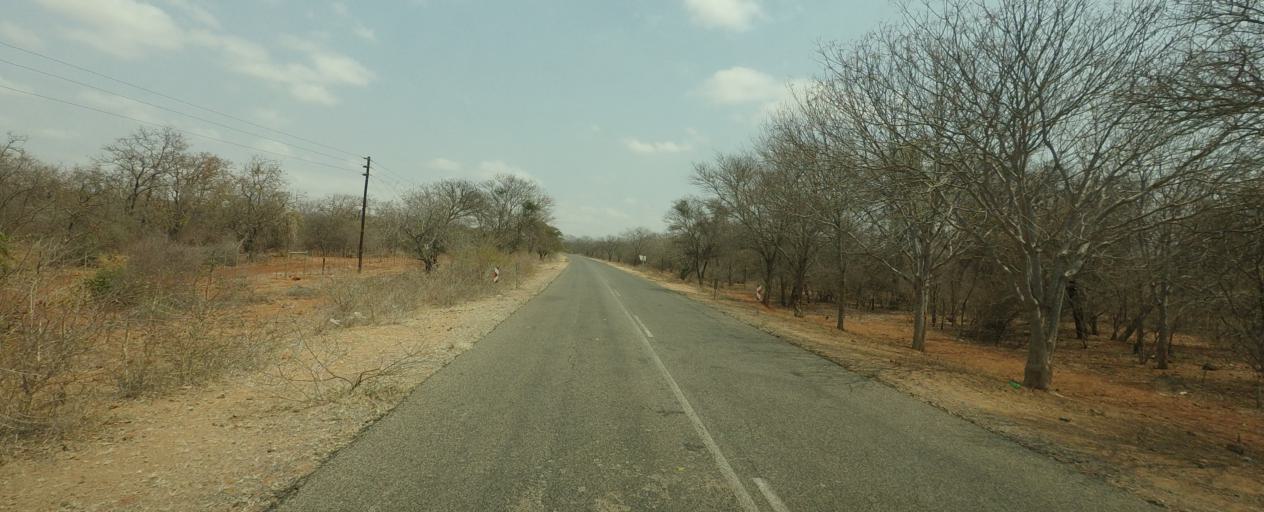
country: ZA
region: Limpopo
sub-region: Vhembe District Municipality
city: Mutale
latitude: -22.4209
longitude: 30.9318
